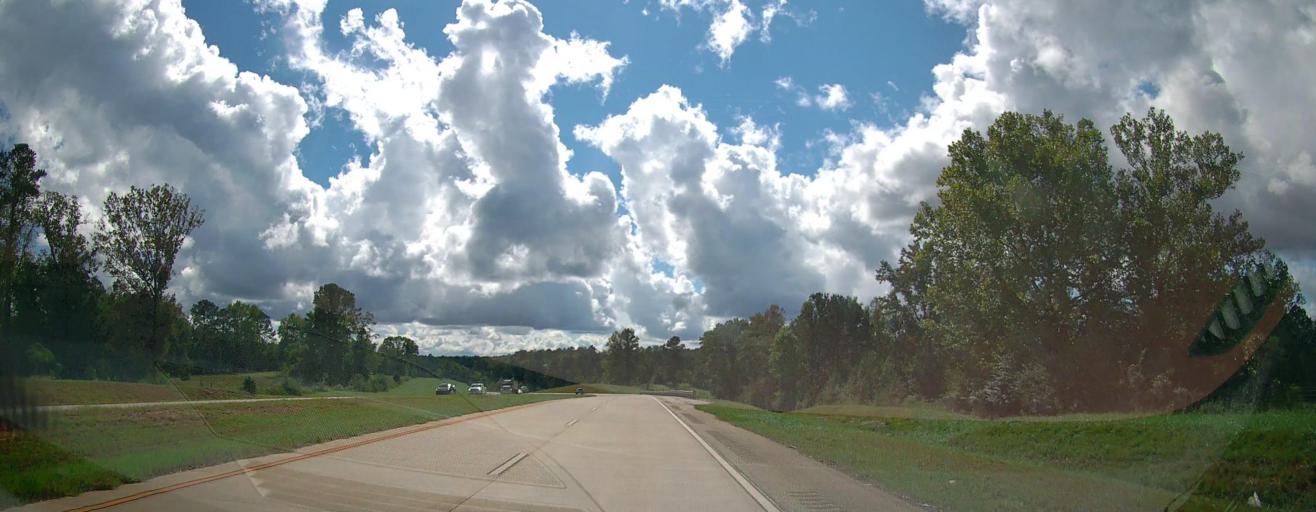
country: US
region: Georgia
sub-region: Jones County
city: Gray
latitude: 33.0120
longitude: -83.5717
